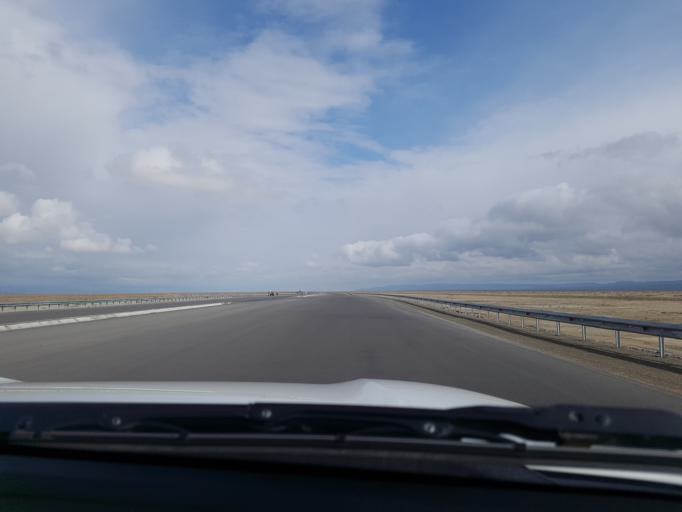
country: TM
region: Balkan
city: Gumdag
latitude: 39.1786
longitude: 54.9537
